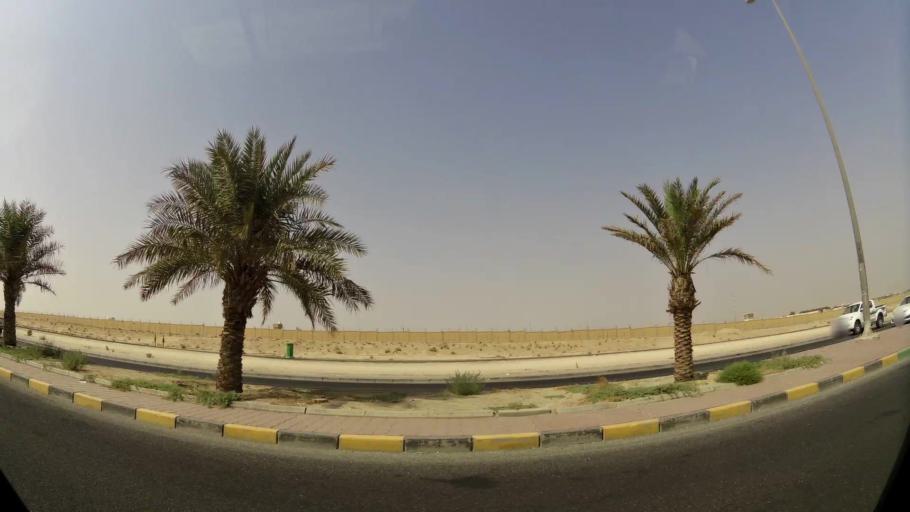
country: KW
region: Muhafazat al Jahra'
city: Al Jahra'
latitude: 29.3129
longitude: 47.7084
